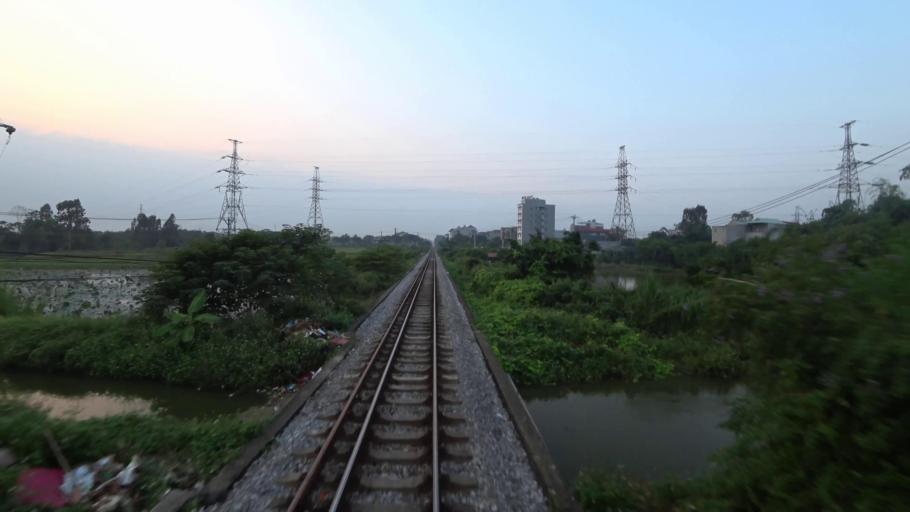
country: VN
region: Ha Noi
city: Dong Anh
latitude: 21.1475
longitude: 105.8588
